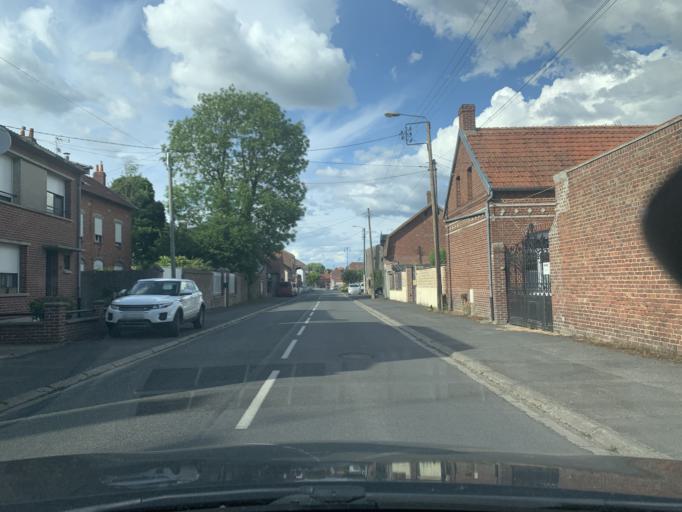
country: FR
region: Nord-Pas-de-Calais
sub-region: Departement du Nord
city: Marcoing
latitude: 50.1195
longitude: 3.1709
